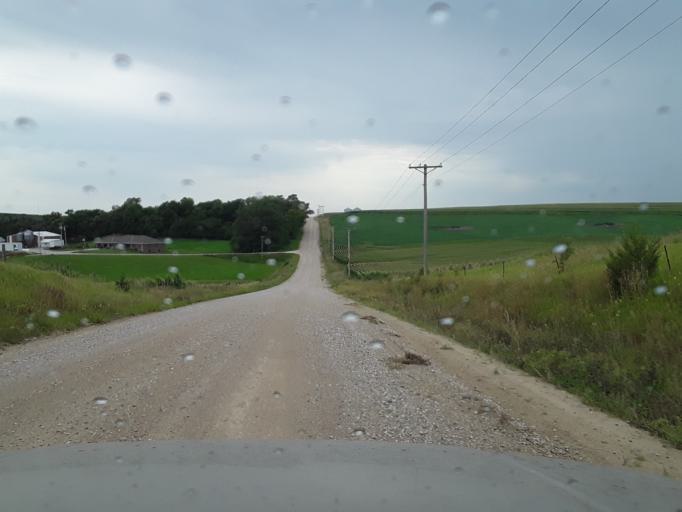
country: US
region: Nebraska
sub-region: Washington County
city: Blair
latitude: 41.5092
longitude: -96.1797
